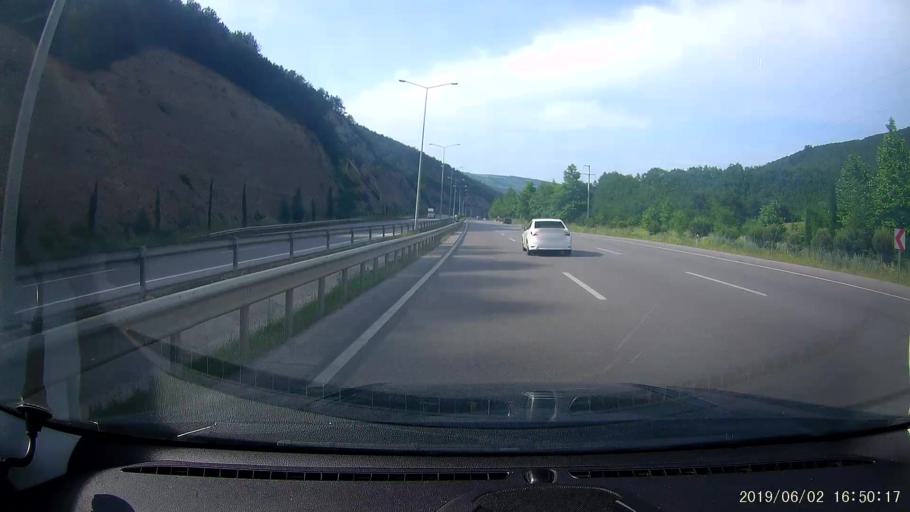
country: TR
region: Samsun
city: Samsun
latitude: 41.2515
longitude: 36.1736
